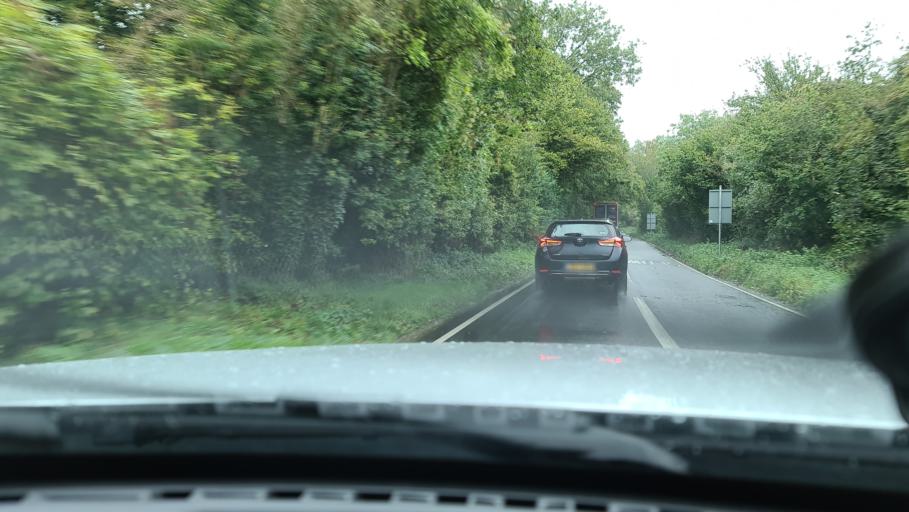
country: GB
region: England
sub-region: Oxfordshire
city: Woodstock
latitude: 51.8753
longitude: -1.3531
